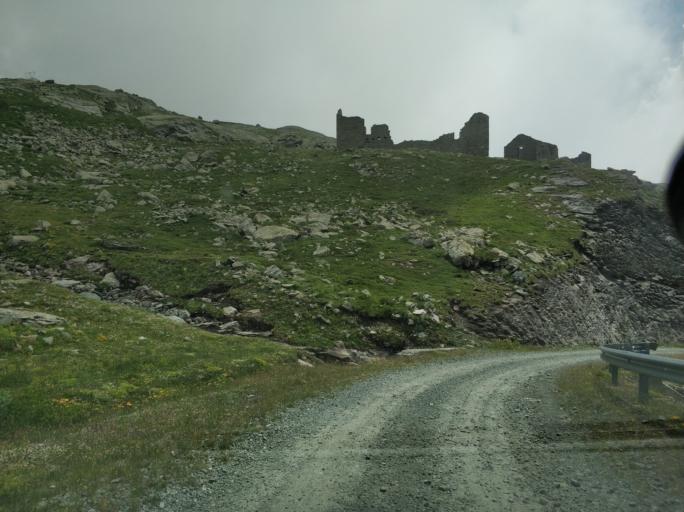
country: IT
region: Piedmont
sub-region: Provincia di Torino
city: Usseglio
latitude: 45.2593
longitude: 7.1657
